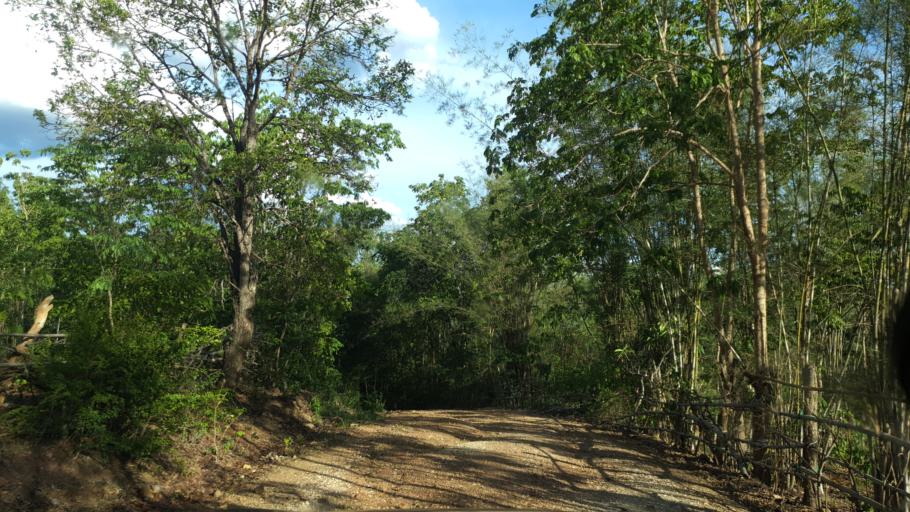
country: TH
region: Lampang
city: Sop Prap
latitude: 17.8832
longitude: 99.2930
